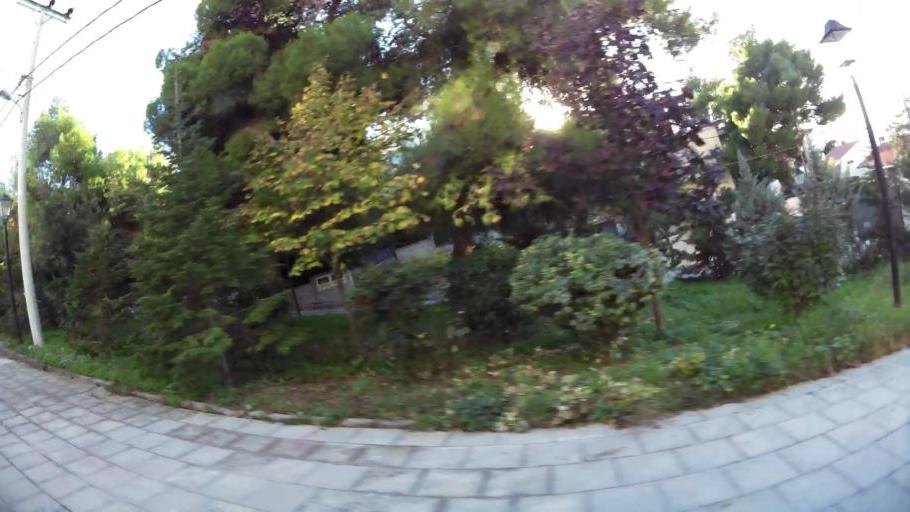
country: GR
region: Attica
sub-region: Nomarchia Athinas
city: Ekali
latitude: 38.0924
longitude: 23.8341
